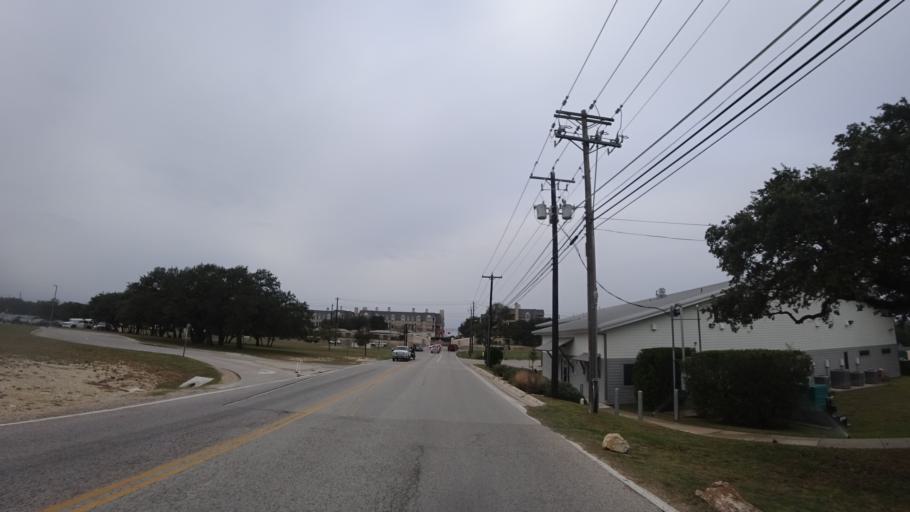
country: US
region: Texas
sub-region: Travis County
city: Hudson Bend
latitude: 30.3922
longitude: -97.9345
